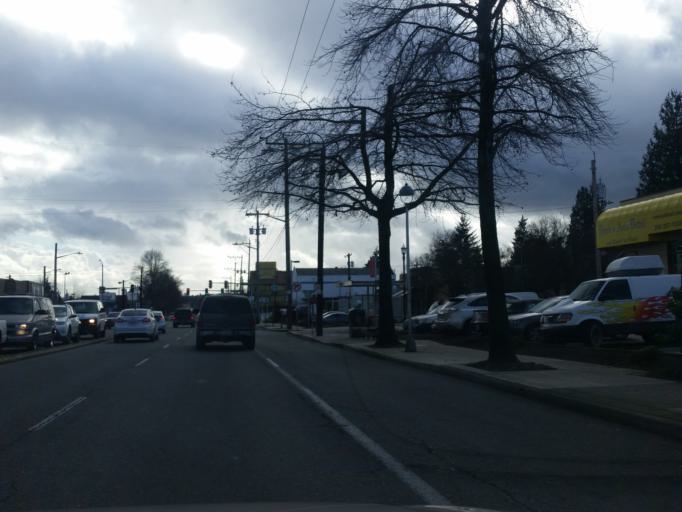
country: US
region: Washington
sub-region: King County
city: Shoreline
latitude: 47.6902
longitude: -122.3446
